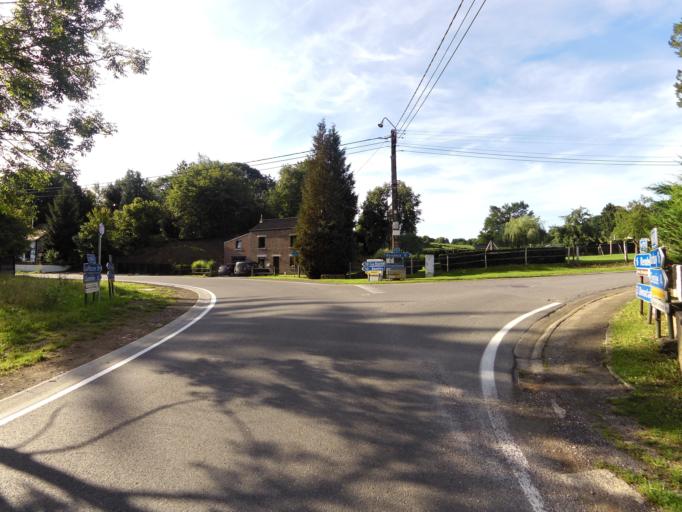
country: BE
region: Wallonia
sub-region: Province du Luxembourg
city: Erezee
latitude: 50.2664
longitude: 5.5616
